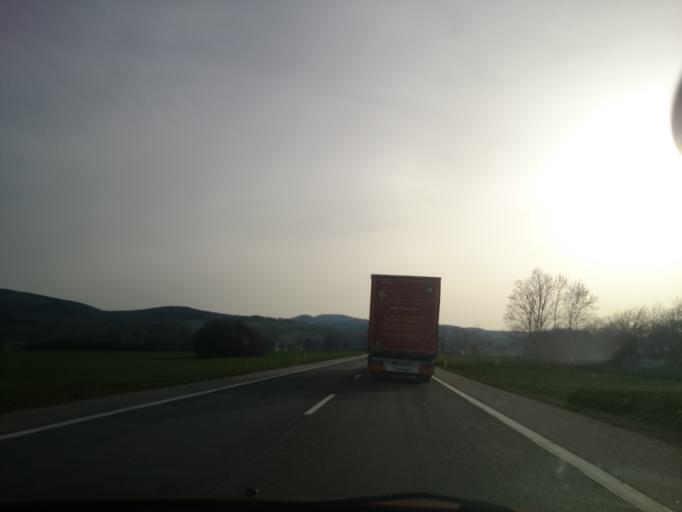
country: PL
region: Opole Voivodeship
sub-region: Powiat nyski
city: Kamienica
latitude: 50.4519
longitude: 16.9215
